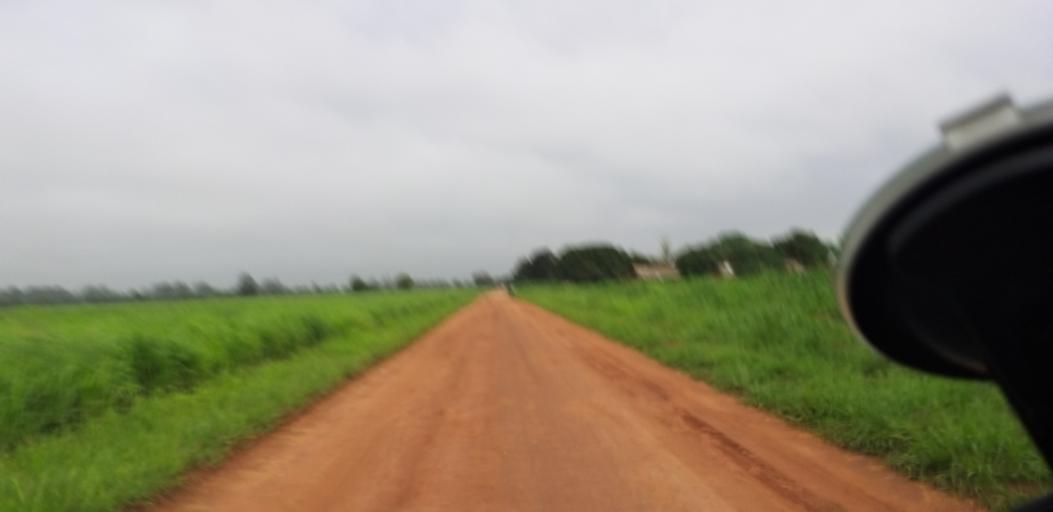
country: ZM
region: Lusaka
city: Lusaka
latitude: -15.5239
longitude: 28.3035
